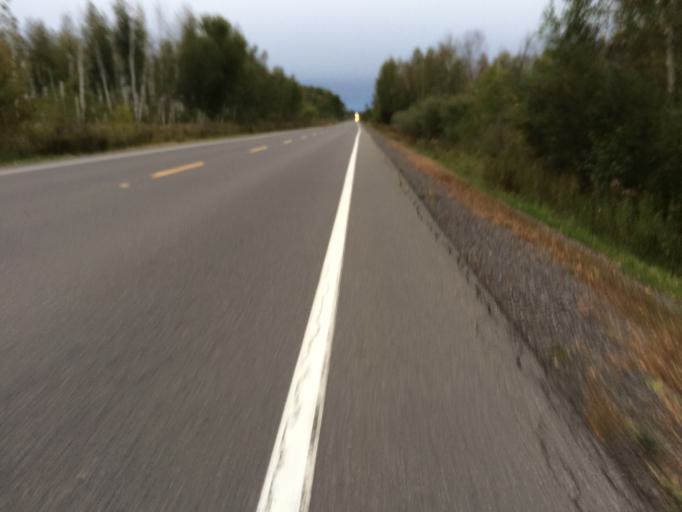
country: CA
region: Ontario
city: Ottawa
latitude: 45.3042
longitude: -75.6422
